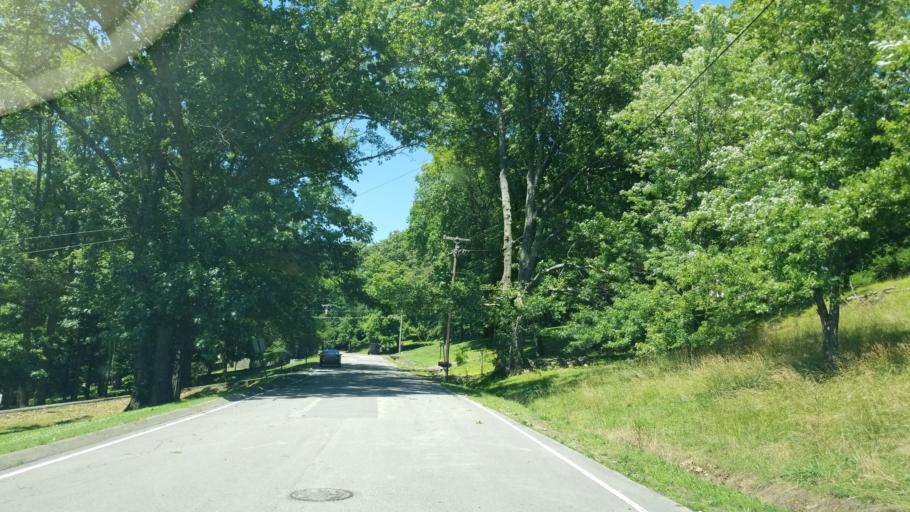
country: US
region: Tennessee
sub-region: Davidson County
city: Forest Hills
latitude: 36.0591
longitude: -86.8122
